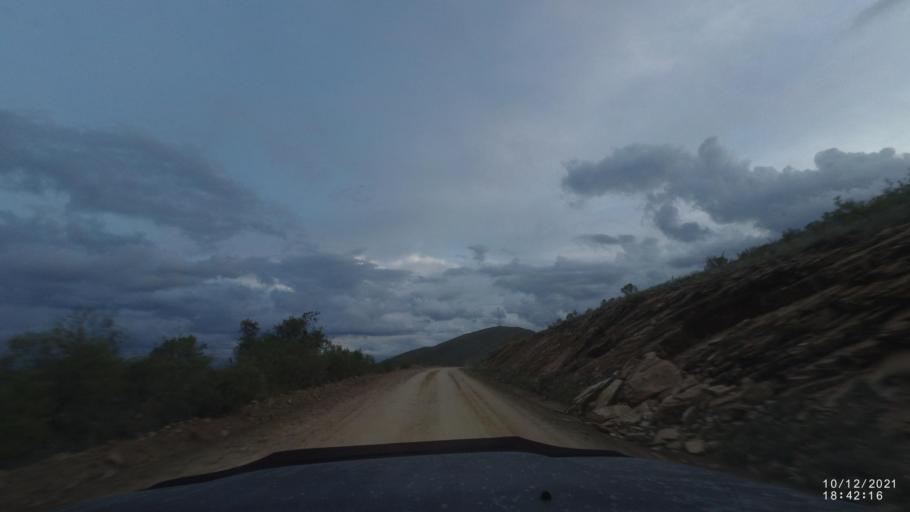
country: BO
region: Cochabamba
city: Tarata
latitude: -17.8681
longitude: -65.9848
